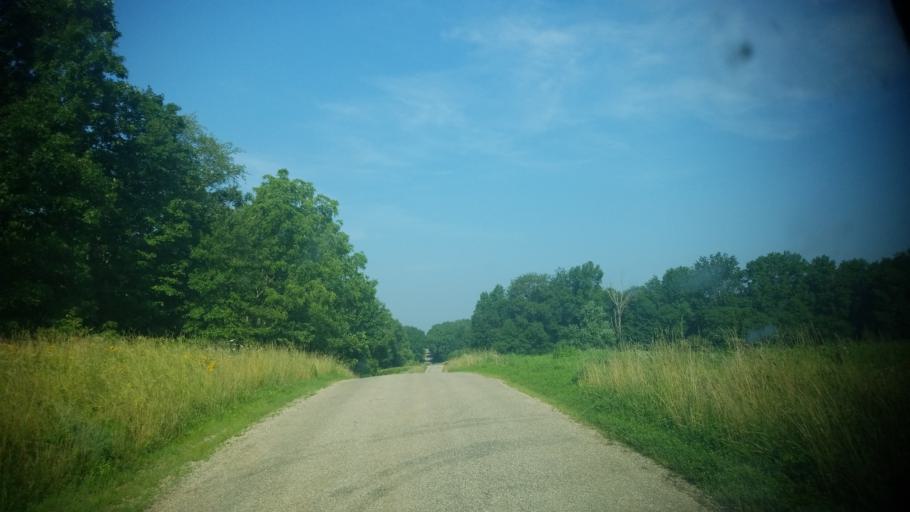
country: US
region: Illinois
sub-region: Clay County
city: Flora
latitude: 38.6028
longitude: -88.4131
